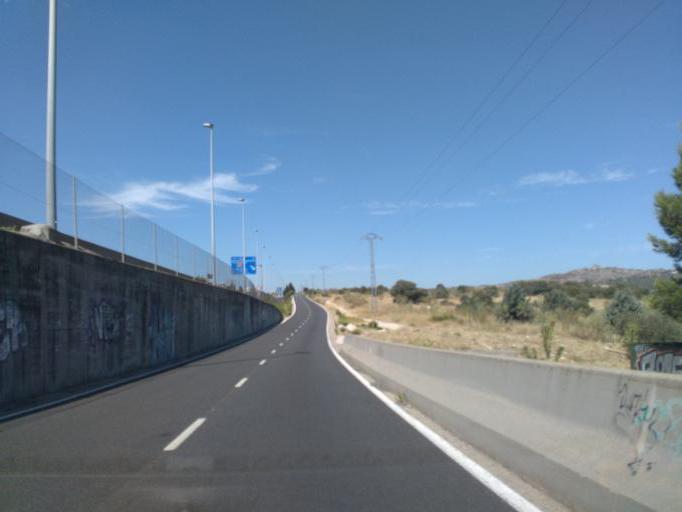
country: ES
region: Madrid
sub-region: Provincia de Madrid
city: Las Matas
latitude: 40.5638
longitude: -3.9064
